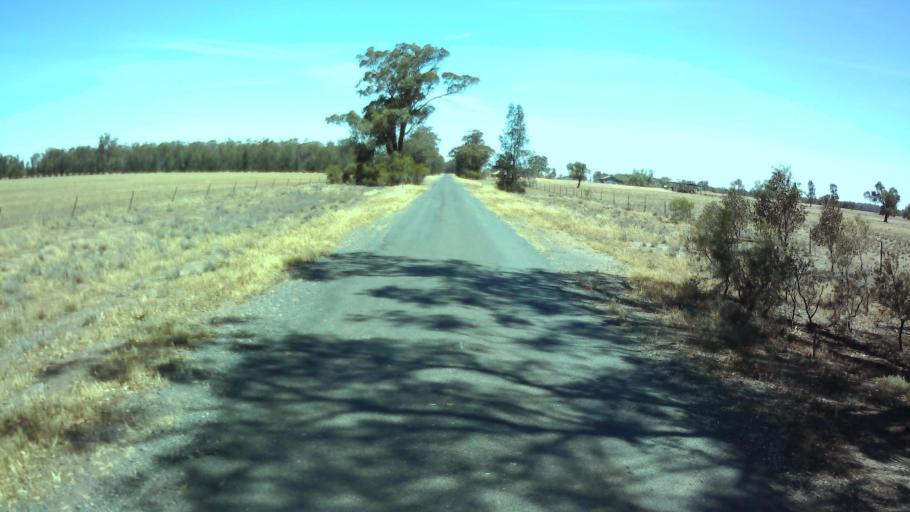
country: AU
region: New South Wales
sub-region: Weddin
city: Grenfell
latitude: -33.9003
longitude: 147.6865
